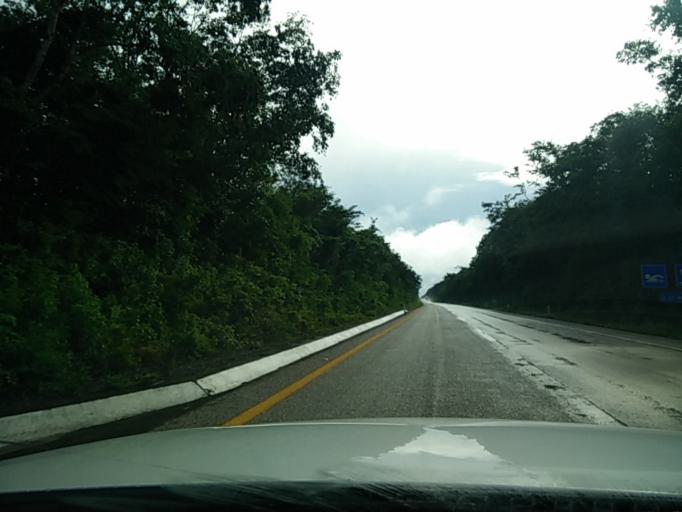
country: MX
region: Yucatan
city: Tunkas
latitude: 20.7614
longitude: -88.7819
